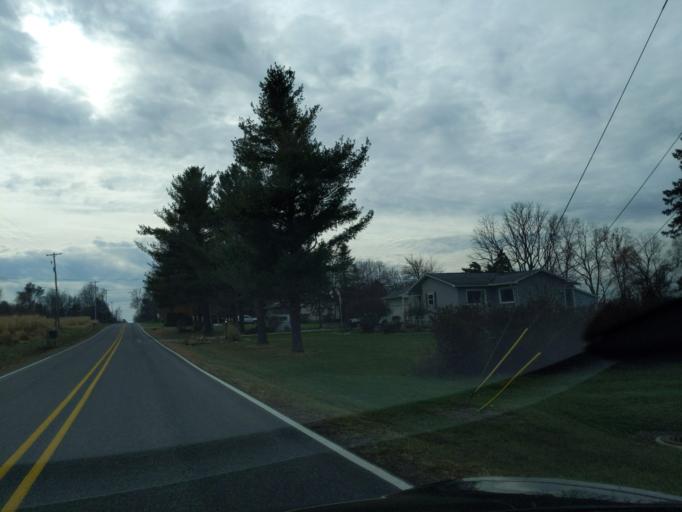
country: US
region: Michigan
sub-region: Ingham County
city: Mason
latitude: 42.5213
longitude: -84.5224
